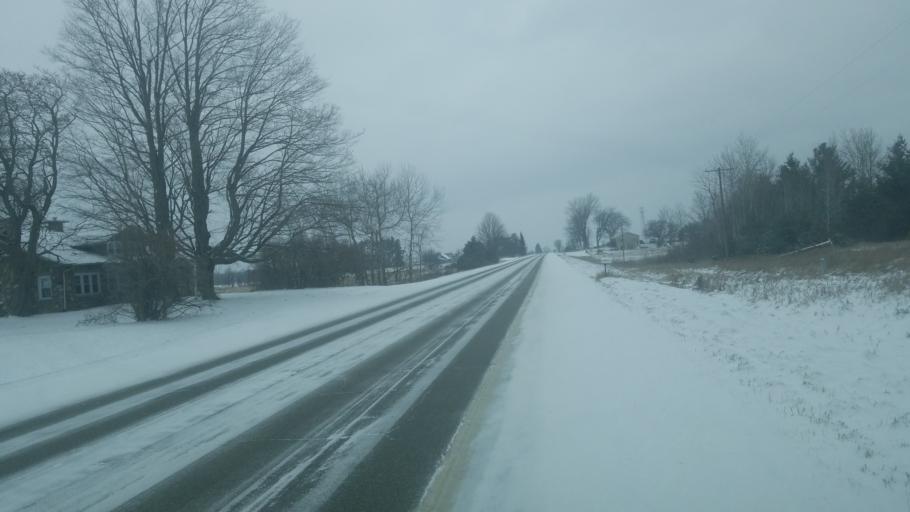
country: US
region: Michigan
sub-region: Osceola County
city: Evart
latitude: 43.9065
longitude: -85.1478
